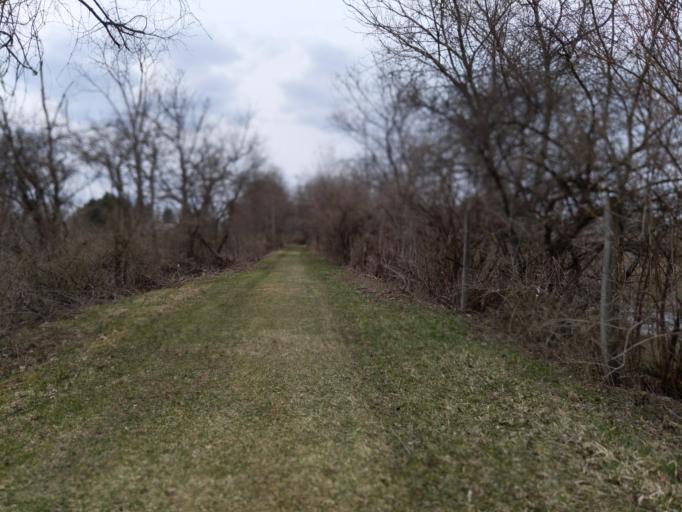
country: US
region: New York
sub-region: Tompkins County
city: Dryden
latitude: 42.4973
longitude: -76.3254
